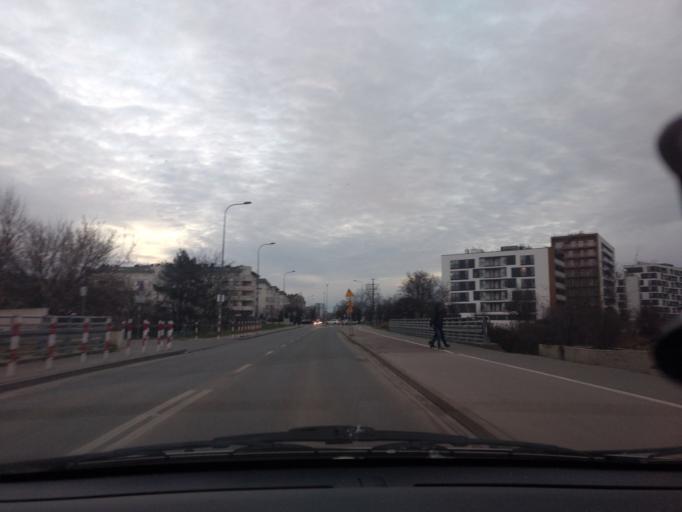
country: PL
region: Masovian Voivodeship
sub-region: Warszawa
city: Praga Poludnie
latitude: 52.2300
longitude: 21.0804
